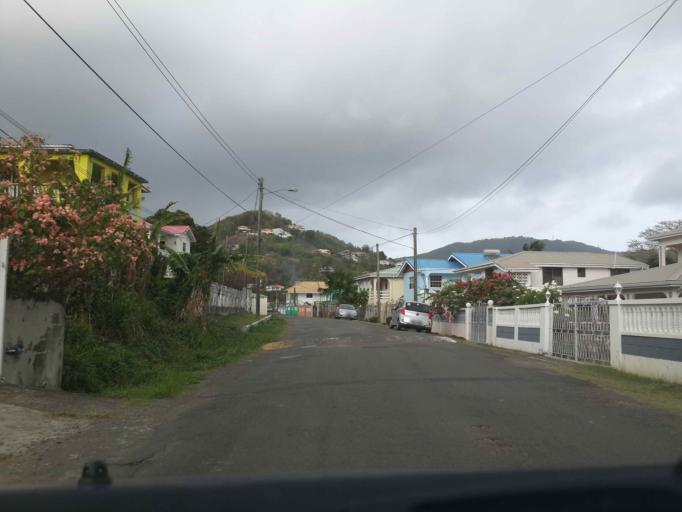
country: LC
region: Gros-Islet
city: Gros Islet
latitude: 14.0453
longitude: -60.9604
